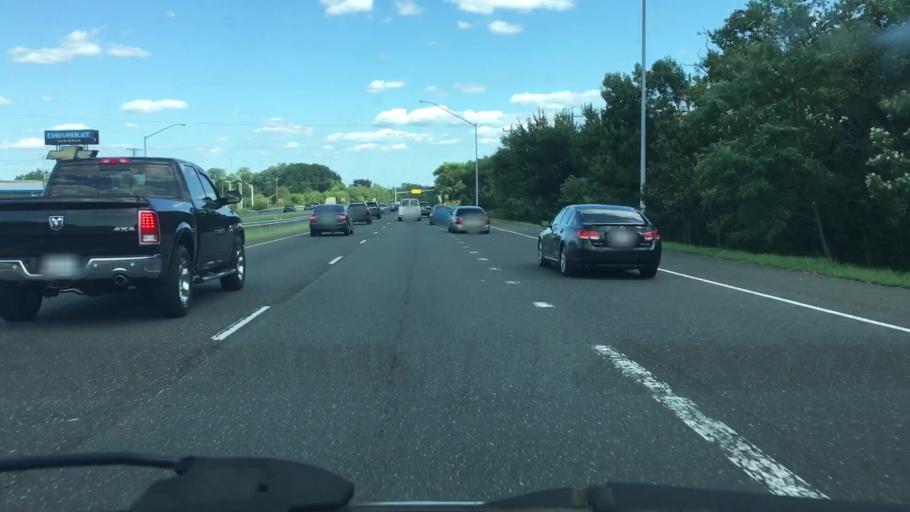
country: US
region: Maryland
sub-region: Prince George's County
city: Silver Hill
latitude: 38.8312
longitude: -76.9365
